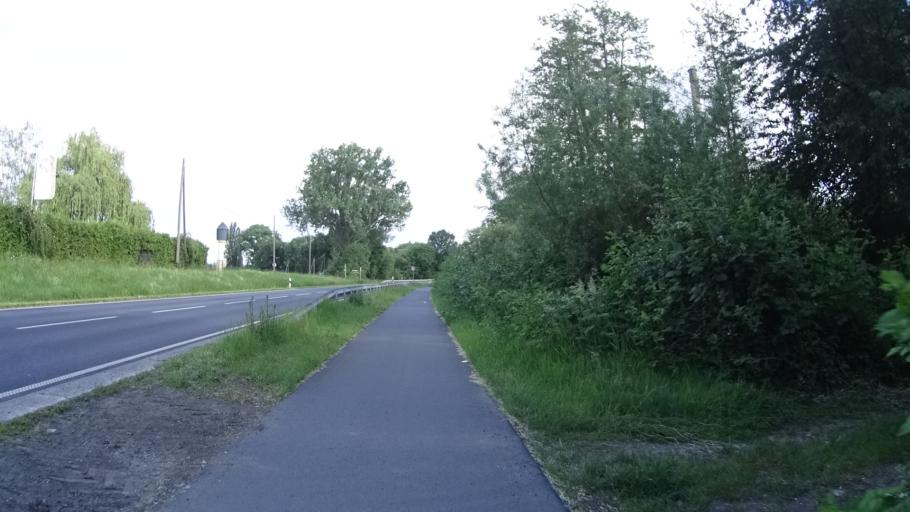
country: DE
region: Hesse
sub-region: Regierungsbezirk Darmstadt
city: Grosskrotzenburg
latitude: 50.0926
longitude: 8.9526
